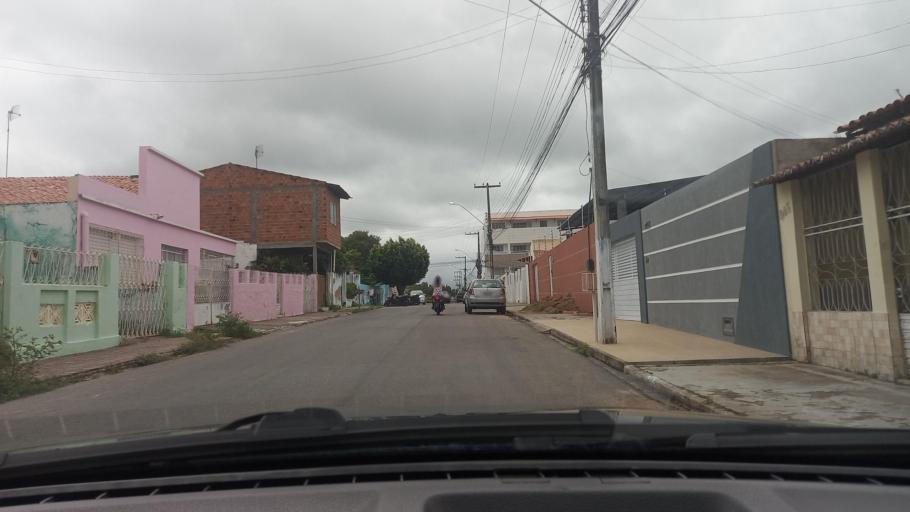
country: BR
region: Alagoas
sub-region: Delmiro Gouveia
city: Delmiro Gouveia
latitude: -9.3877
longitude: -37.9979
